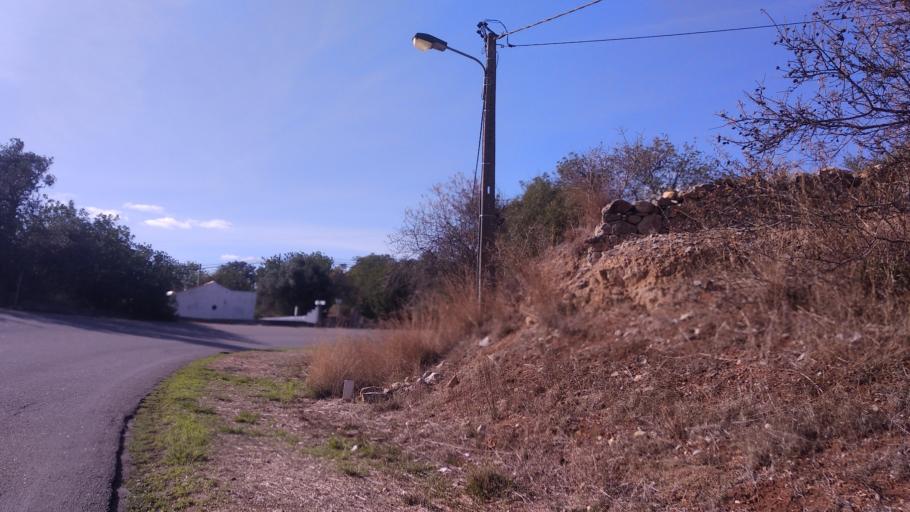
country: PT
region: Faro
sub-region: Sao Bras de Alportel
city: Sao Bras de Alportel
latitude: 37.1591
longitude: -7.8984
